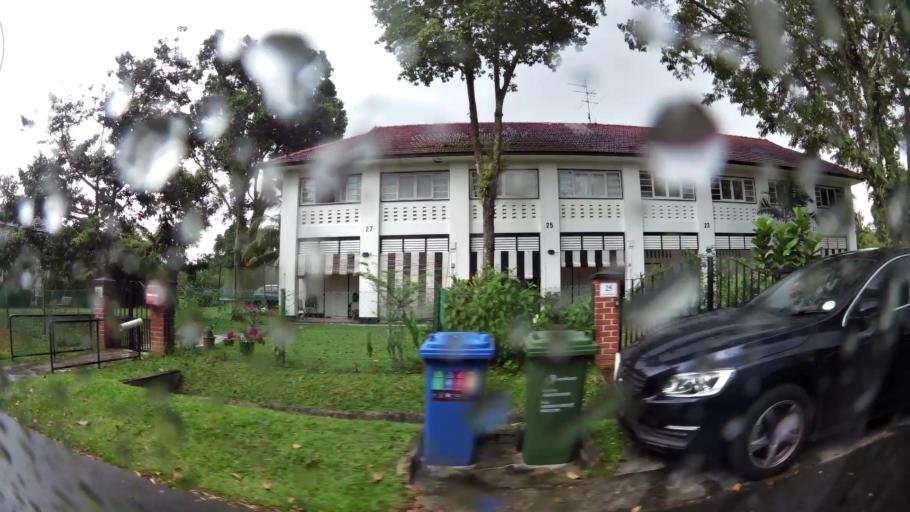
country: MY
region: Johor
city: Kampung Pasir Gudang Baru
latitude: 1.4067
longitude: 103.8703
